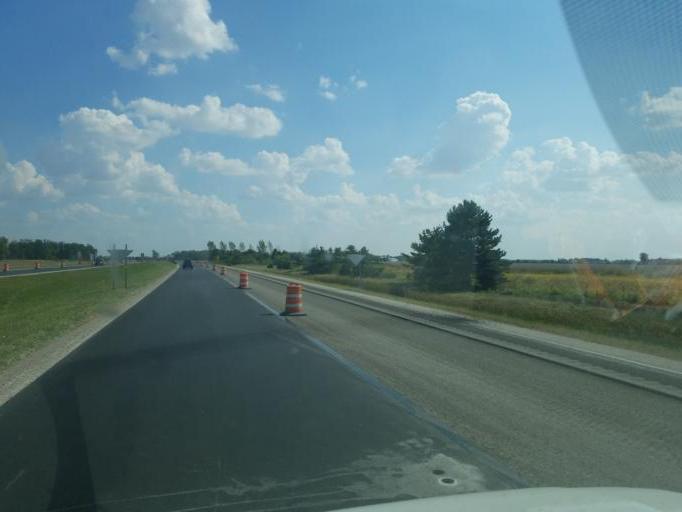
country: US
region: Ohio
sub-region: Van Wert County
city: Convoy
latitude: 40.9043
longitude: -84.6535
